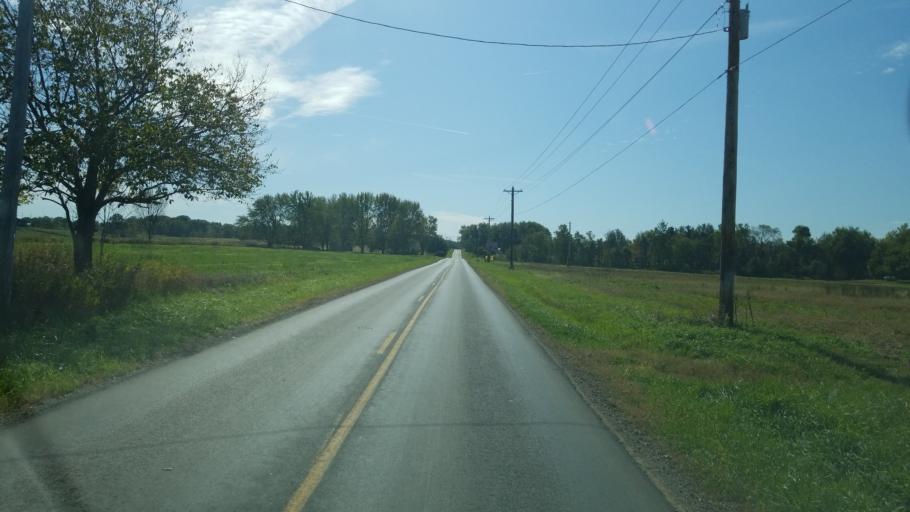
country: US
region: Ohio
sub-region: Wayne County
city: West Salem
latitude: 41.0213
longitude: -82.1264
